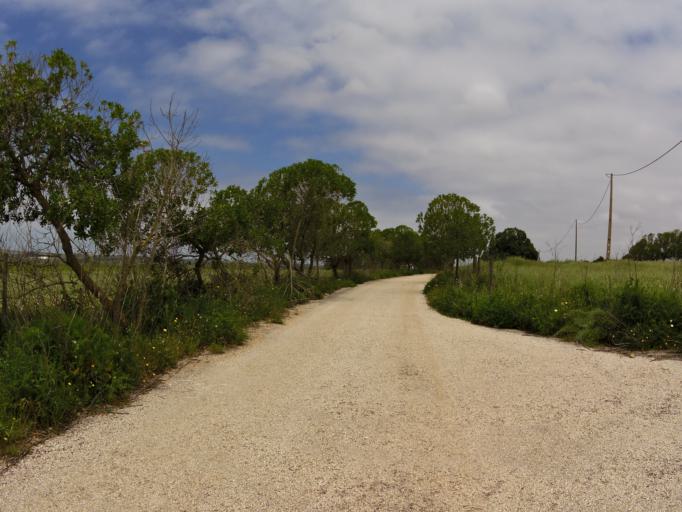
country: PT
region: Faro
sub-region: Vila do Bispo
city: Vila do Bispo
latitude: 37.0790
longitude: -8.8794
